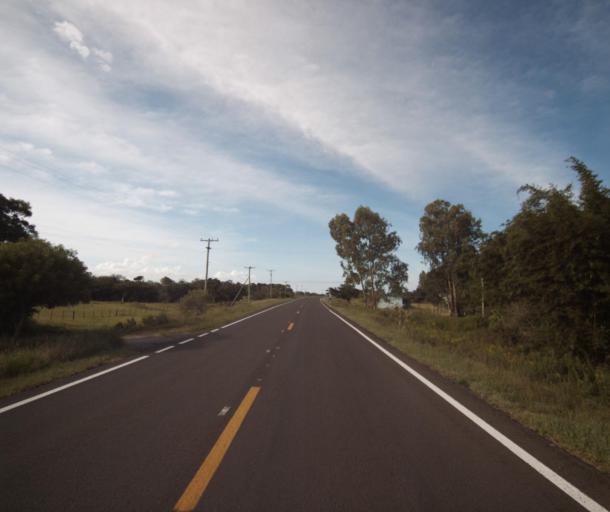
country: BR
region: Rio Grande do Sul
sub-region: Tapes
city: Tapes
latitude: -31.3251
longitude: -51.1252
